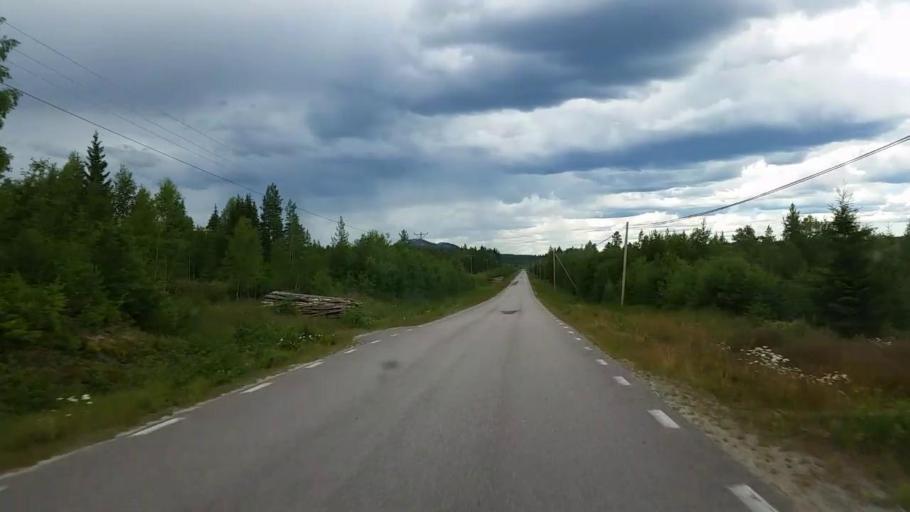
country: SE
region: Gaevleborg
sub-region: Ovanakers Kommun
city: Edsbyn
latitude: 61.4395
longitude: 15.8917
